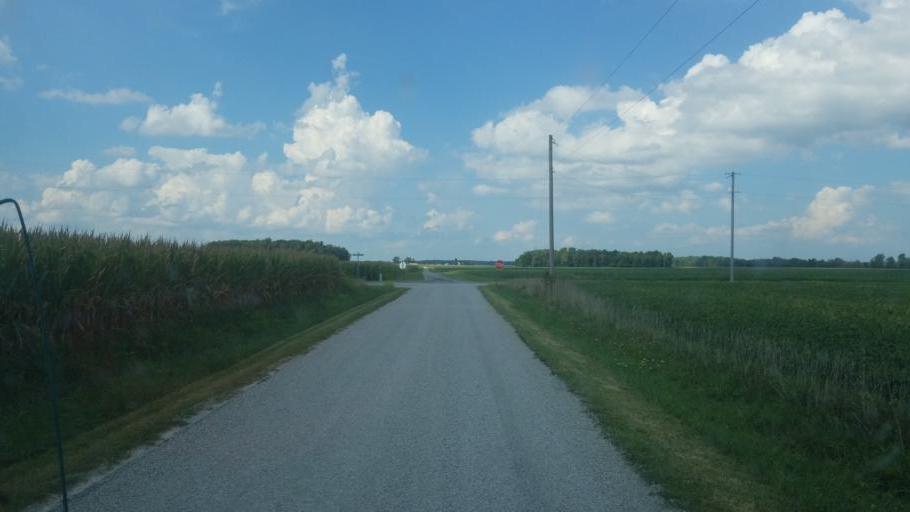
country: US
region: Ohio
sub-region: Huron County
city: Willard
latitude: 40.9956
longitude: -82.7965
